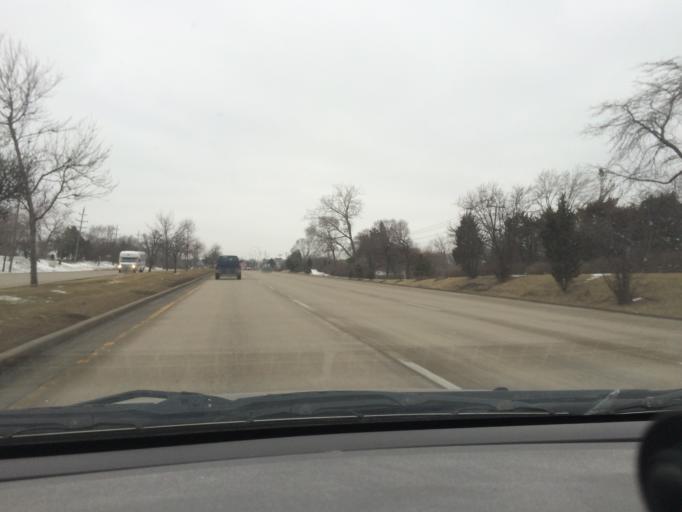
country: US
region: Illinois
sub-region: Cook County
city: Hoffman Estates
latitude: 42.0435
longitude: -88.0732
